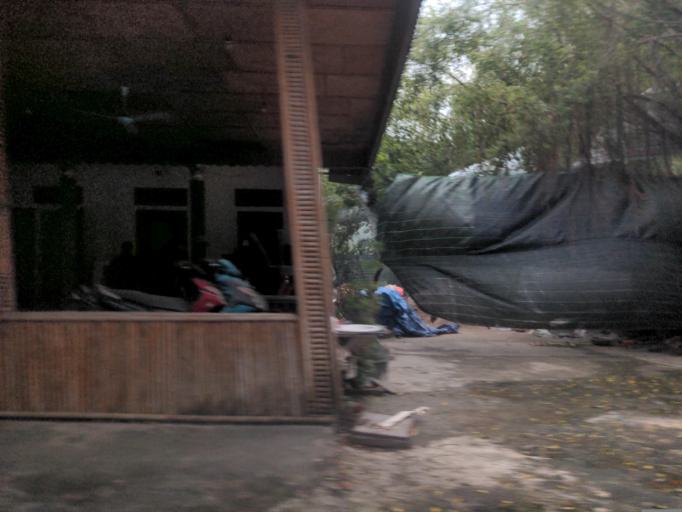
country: VN
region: Ninh Binh
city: Thi Tran Tam Diep
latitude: 20.2181
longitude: 105.9176
